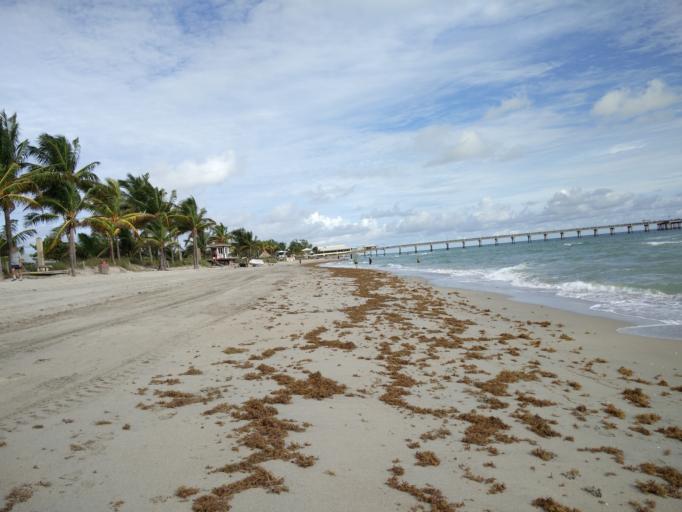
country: US
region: Florida
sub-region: Broward County
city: Dania Beach
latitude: 26.0543
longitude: -80.1117
